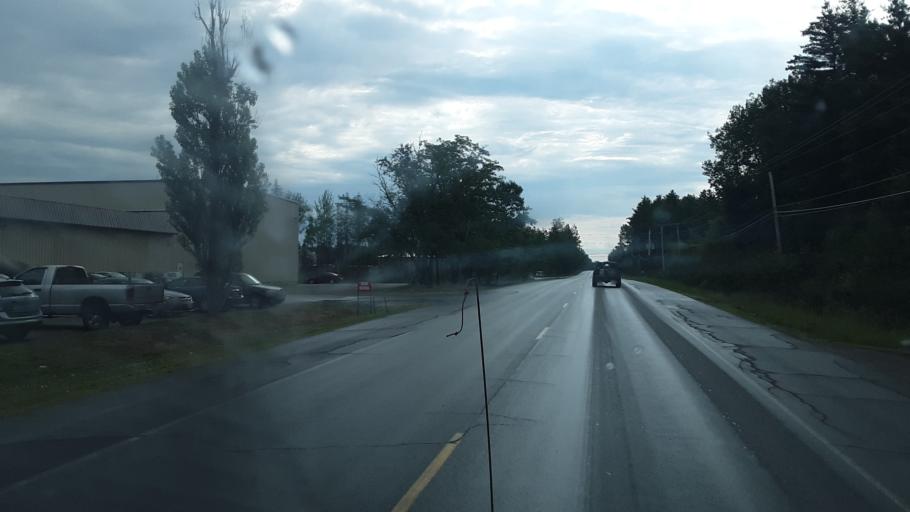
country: US
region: Maine
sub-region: Penobscot County
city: Old Town
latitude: 44.9432
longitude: -68.6724
